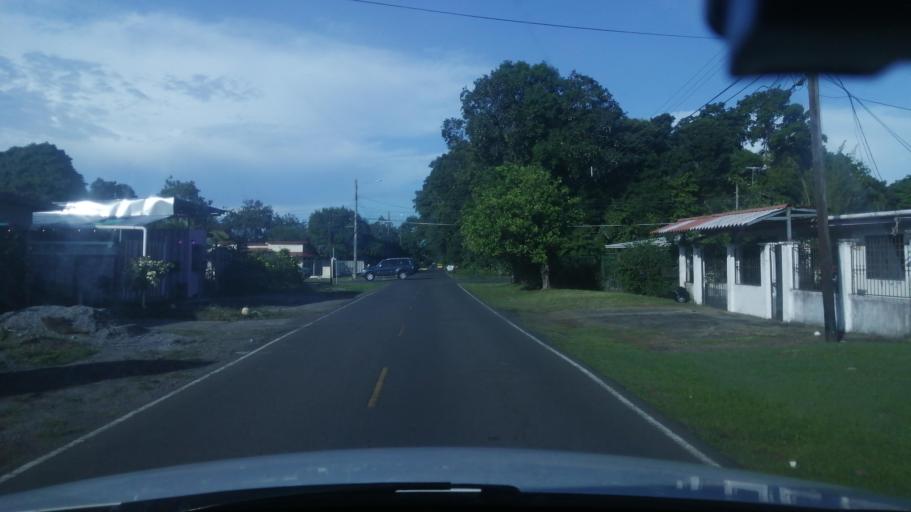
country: PA
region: Chiriqui
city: David
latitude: 8.4372
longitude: -82.4323
